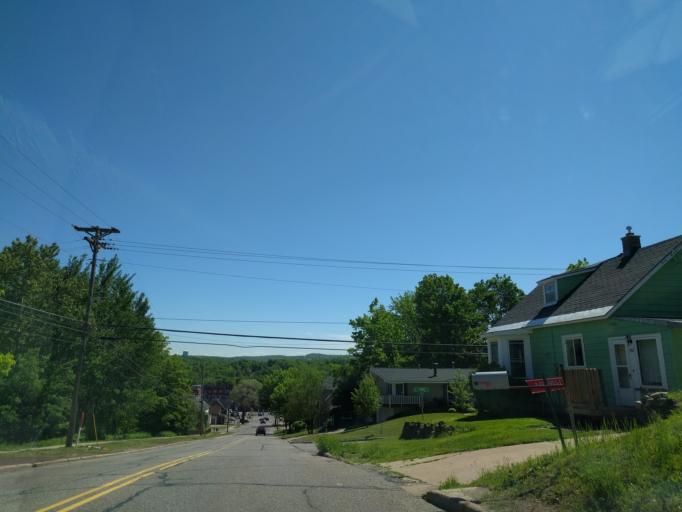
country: US
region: Michigan
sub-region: Marquette County
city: Marquette
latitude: 46.5483
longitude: -87.4123
